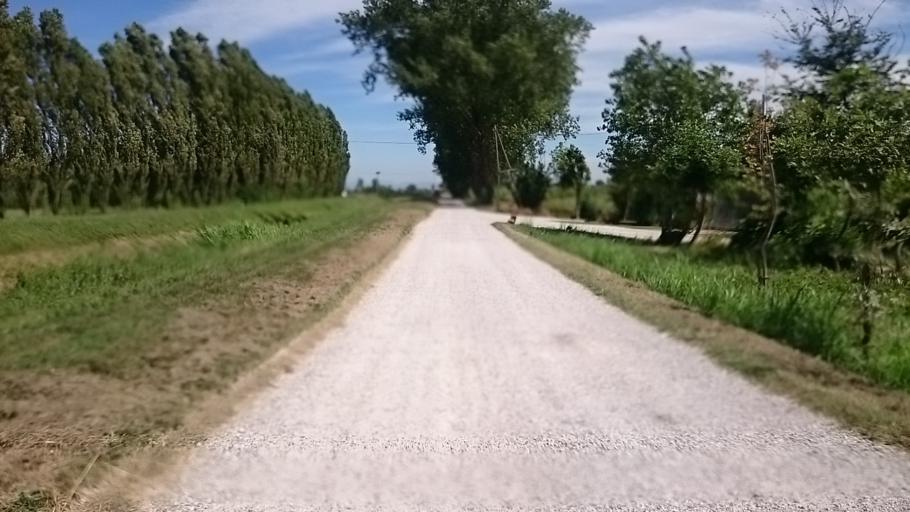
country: IT
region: Veneto
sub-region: Provincia di Padova
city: Pionca
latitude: 45.4545
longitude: 11.9541
